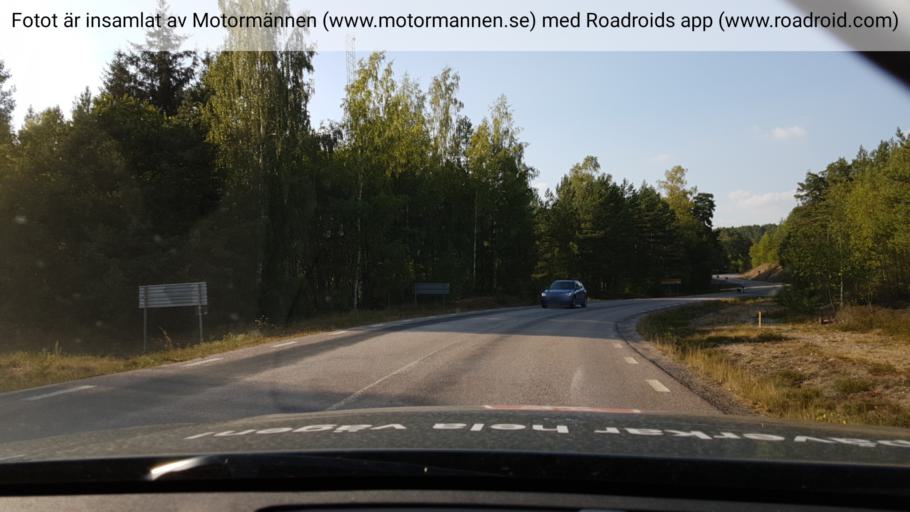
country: SE
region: Soedermanland
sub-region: Strangnas Kommun
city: Mariefred
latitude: 59.1684
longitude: 17.1863
